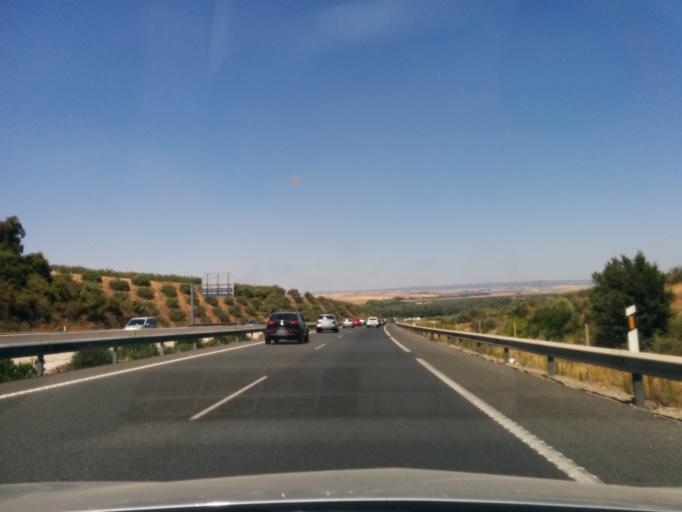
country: ES
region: Andalusia
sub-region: Provincia de Sevilla
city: Benacazon
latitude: 37.3652
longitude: -6.2126
